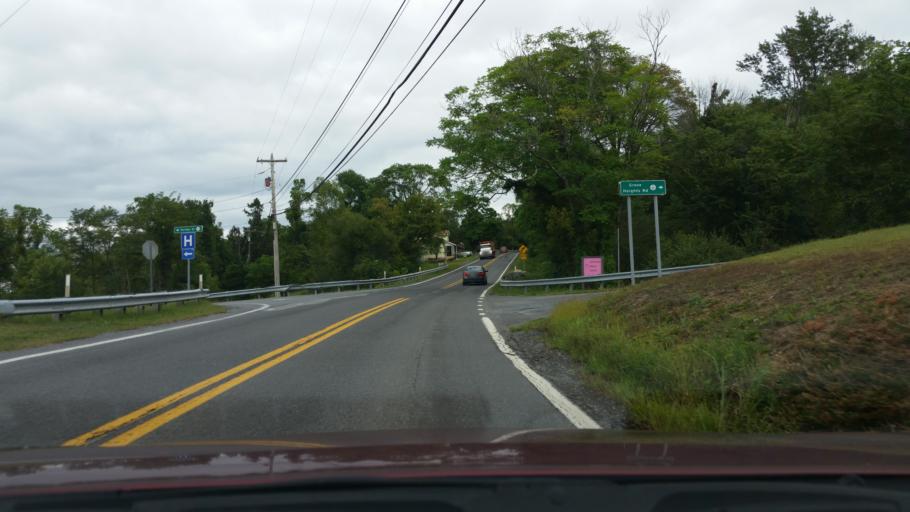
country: US
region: West Virginia
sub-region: Morgan County
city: Berkeley Springs
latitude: 39.6240
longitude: -78.2063
